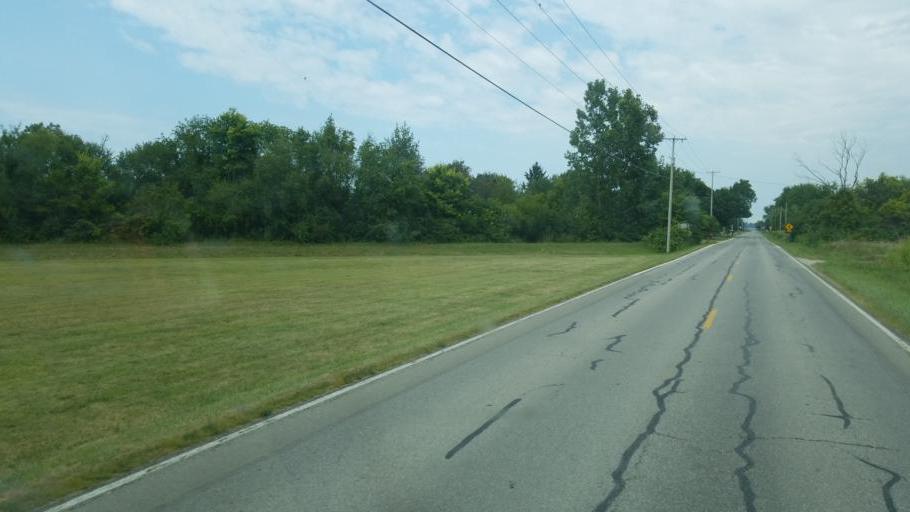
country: US
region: Ohio
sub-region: Marion County
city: Marion
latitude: 40.5678
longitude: -83.1645
